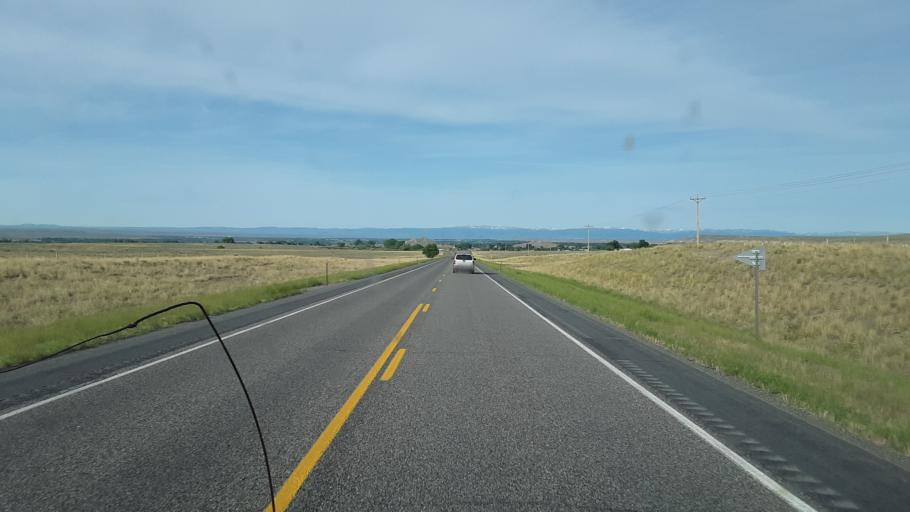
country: US
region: Wyoming
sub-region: Fremont County
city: Riverton
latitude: 43.1474
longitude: -108.2830
